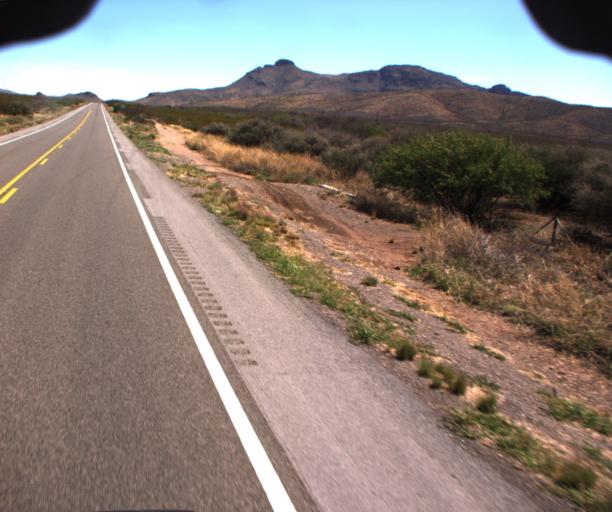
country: US
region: Arizona
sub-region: Cochise County
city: Douglas
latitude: 31.4424
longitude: -109.4751
